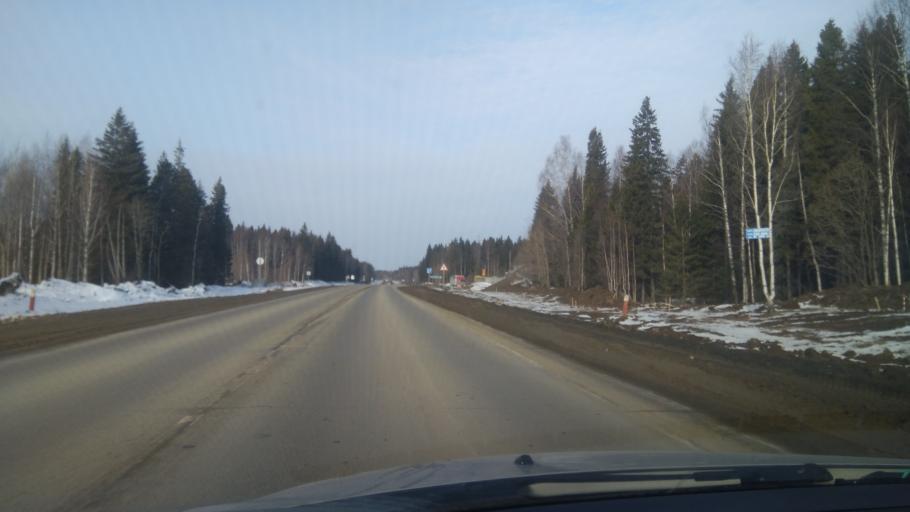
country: RU
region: Sverdlovsk
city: Bisert'
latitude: 56.8266
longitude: 59.1548
